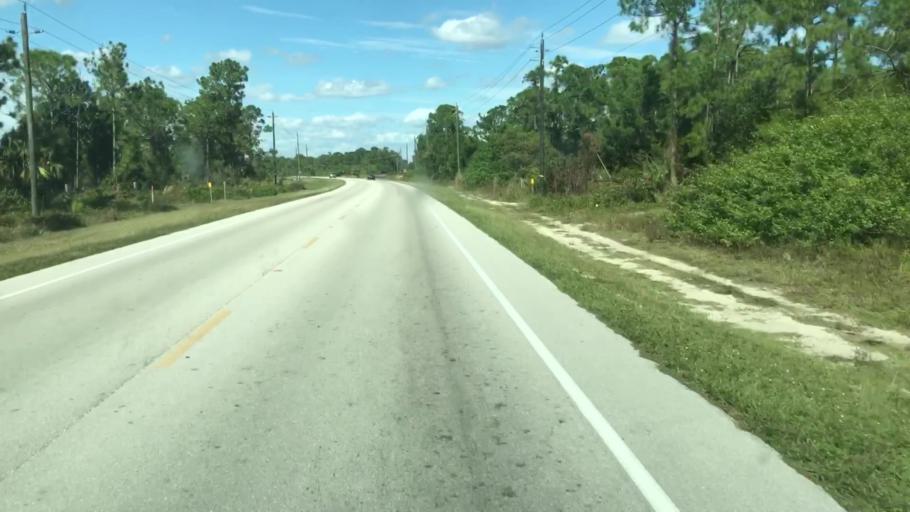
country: US
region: Florida
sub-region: Lee County
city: Alva
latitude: 26.6867
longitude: -81.5986
